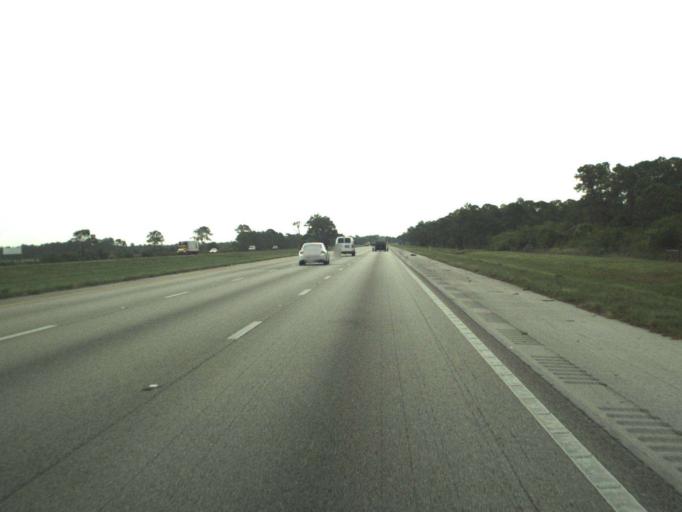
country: US
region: Florida
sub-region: Martin County
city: Palm City
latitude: 27.1268
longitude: -80.3040
